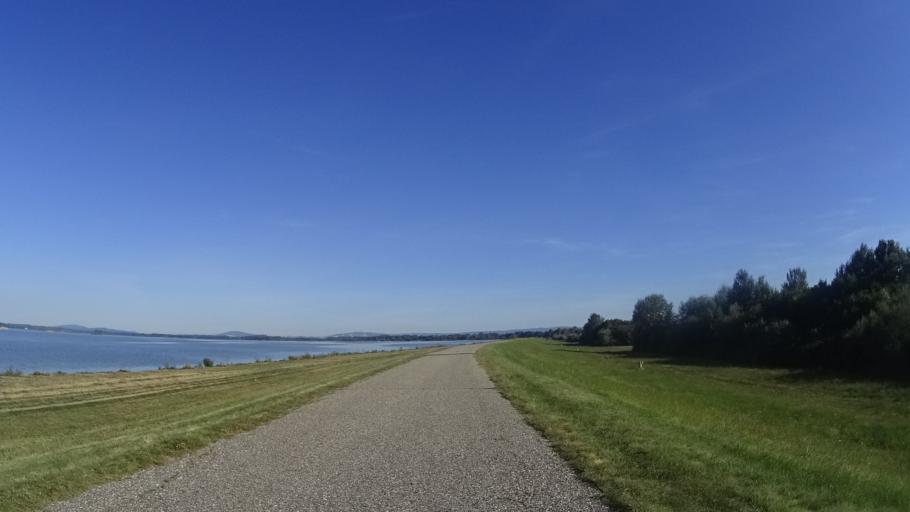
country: SK
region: Bratislavsky
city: Dunajska Luzna
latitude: 48.0362
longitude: 17.2437
